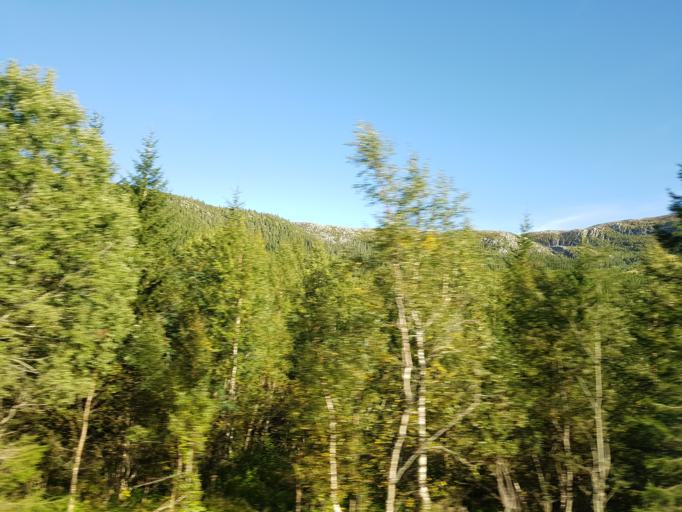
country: NO
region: Sor-Trondelag
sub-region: Afjord
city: A i Afjord
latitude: 63.7287
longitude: 10.2352
